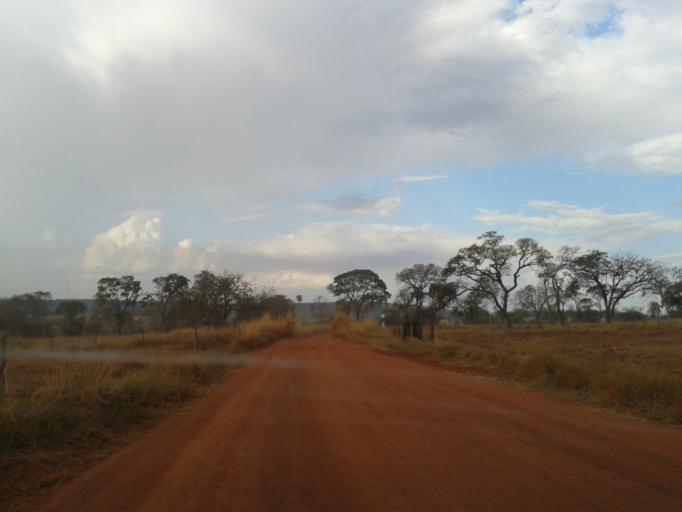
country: BR
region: Minas Gerais
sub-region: Ituiutaba
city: Ituiutaba
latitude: -19.1988
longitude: -49.8364
